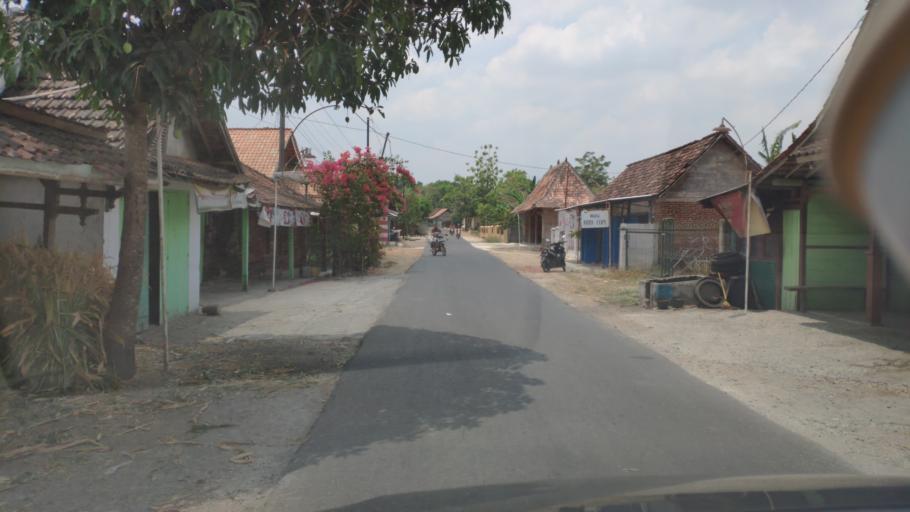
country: ID
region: Central Java
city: Karangtalun
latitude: -7.0190
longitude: 111.3464
